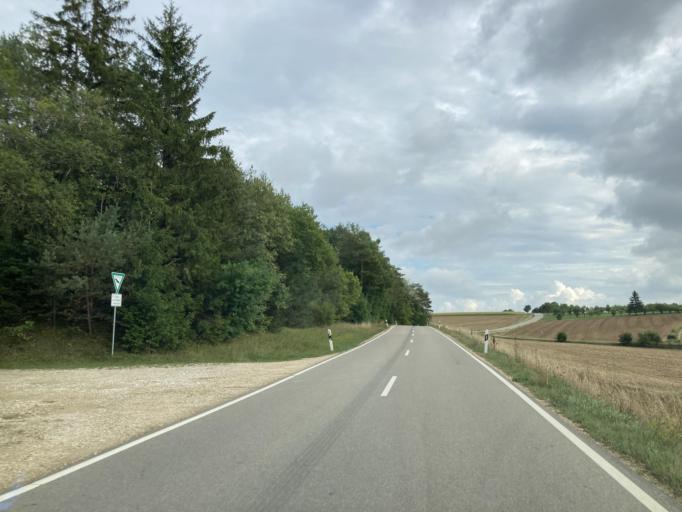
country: DE
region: Bavaria
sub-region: Swabia
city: Forheim
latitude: 48.7725
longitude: 10.4105
